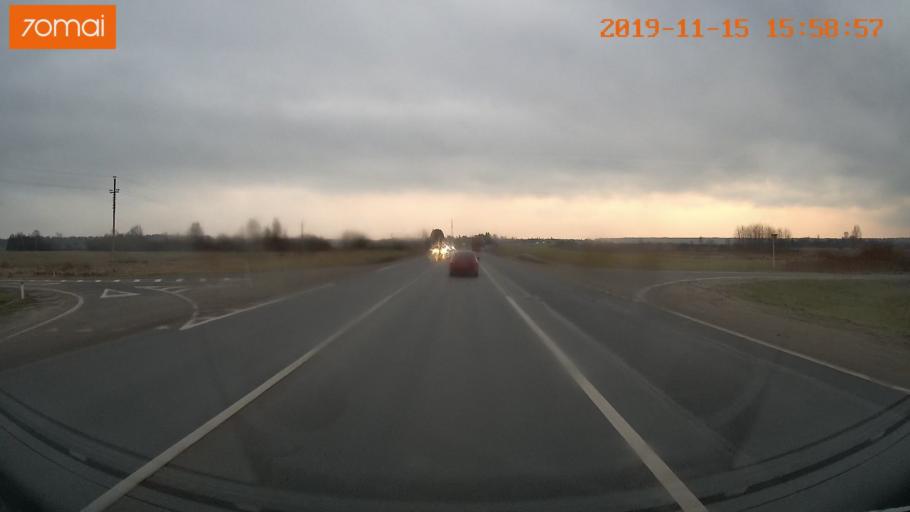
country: RU
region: Jaroslavl
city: Yaroslavl
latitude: 57.8128
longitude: 39.9522
